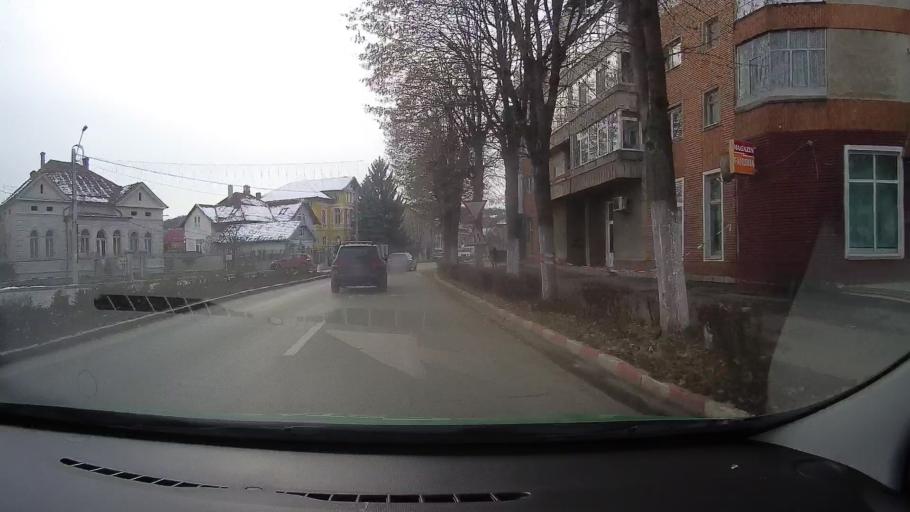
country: RO
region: Hunedoara
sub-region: Municipiul Orastie
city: Orastie
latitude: 45.8379
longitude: 23.1891
